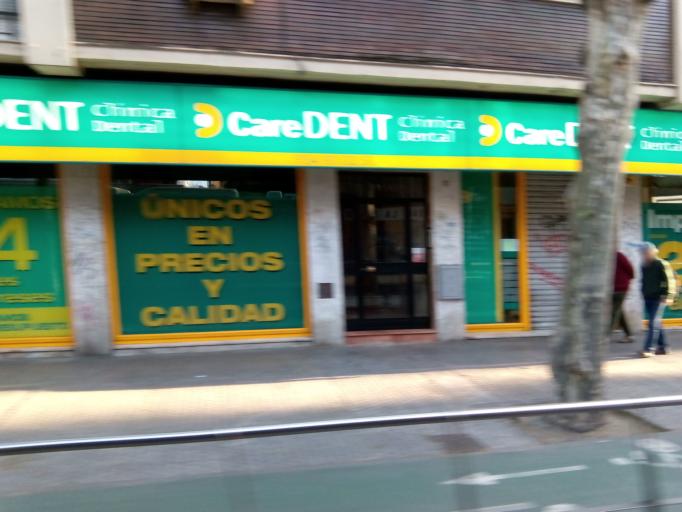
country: ES
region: Andalusia
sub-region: Provincia de Sevilla
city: Sevilla
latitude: 37.4032
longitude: -5.9908
